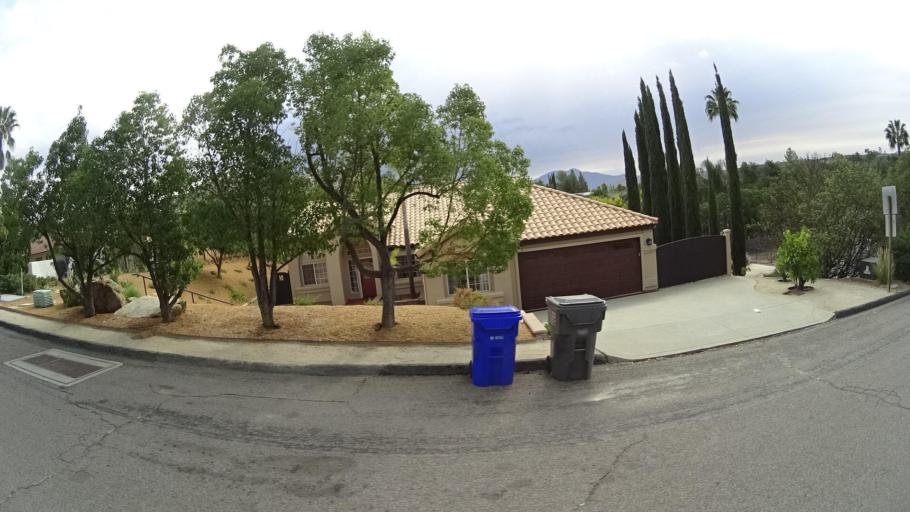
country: US
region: California
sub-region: San Diego County
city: San Diego Country Estates
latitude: 33.0103
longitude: -116.7995
